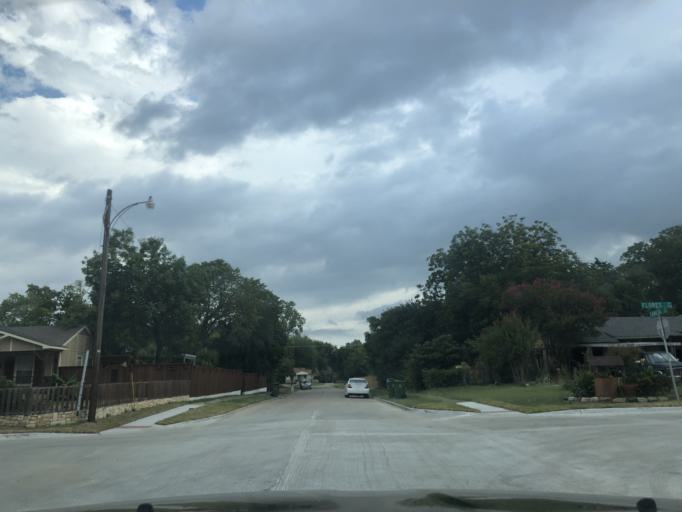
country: US
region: Texas
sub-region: Dallas County
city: Garland
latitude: 32.8813
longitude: -96.6522
